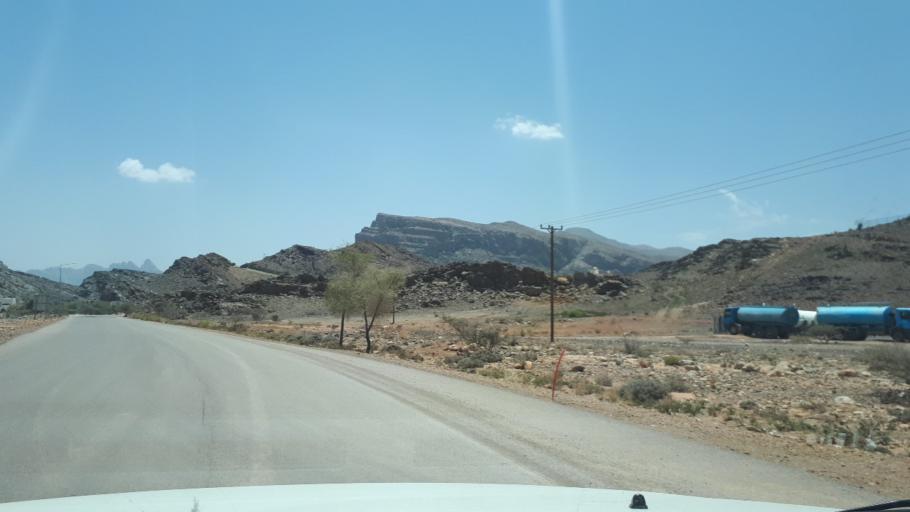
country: OM
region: Muhafazat ad Dakhiliyah
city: Bahla'
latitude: 23.2407
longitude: 57.1500
